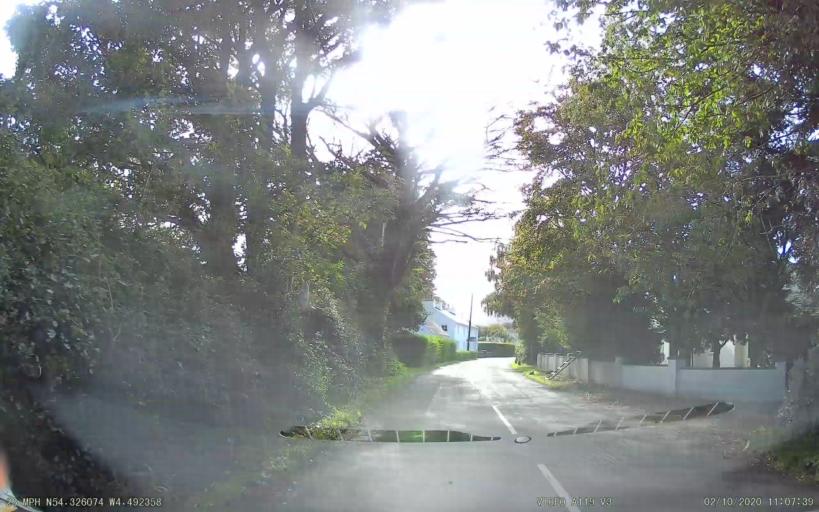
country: IM
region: Ramsey
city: Ramsey
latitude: 54.3261
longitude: -4.4924
